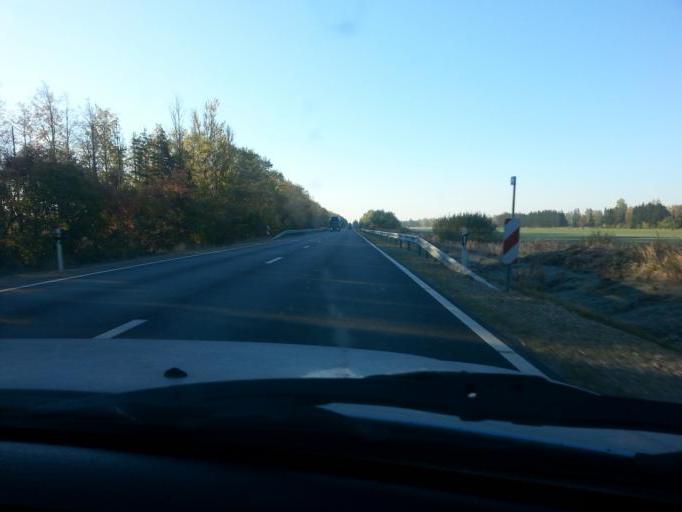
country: LV
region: Jelgava
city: Jelgava
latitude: 56.5185
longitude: 23.7034
